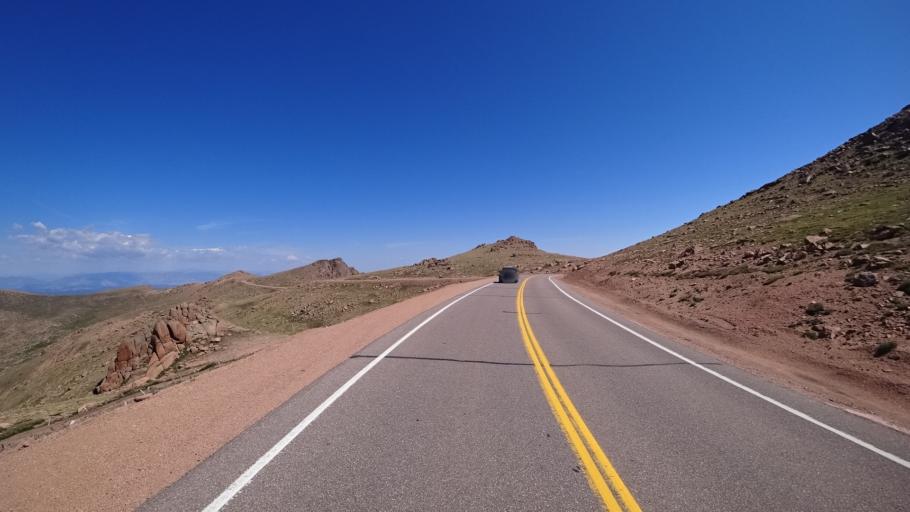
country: US
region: Colorado
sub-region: El Paso County
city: Cascade-Chipita Park
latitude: 38.8494
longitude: -105.0622
